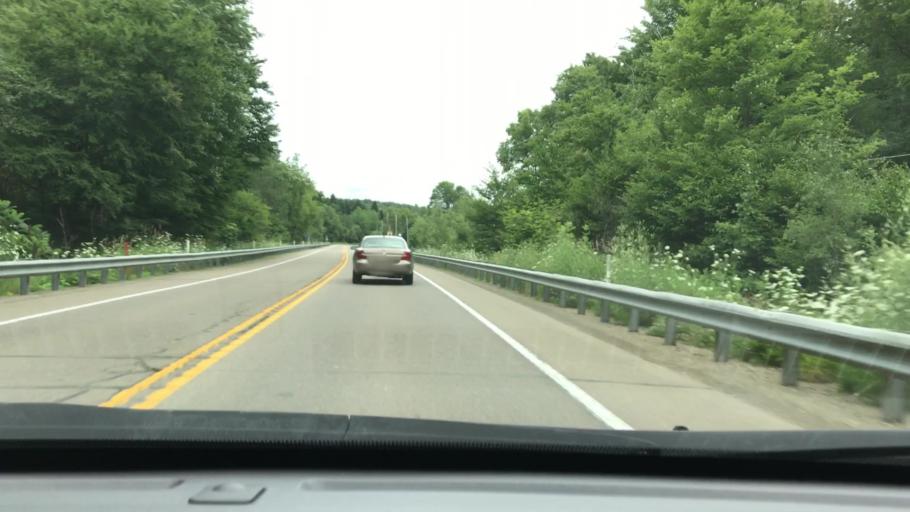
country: US
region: Pennsylvania
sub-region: Elk County
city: Johnsonburg
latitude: 41.5133
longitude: -78.6789
